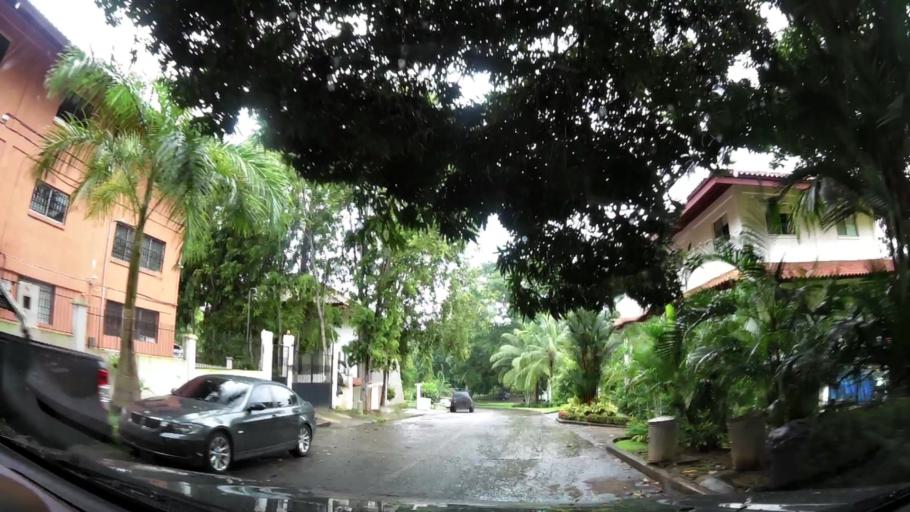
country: PA
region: Panama
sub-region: Distrito de Panama
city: Ancon
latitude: 8.9859
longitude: -79.5585
